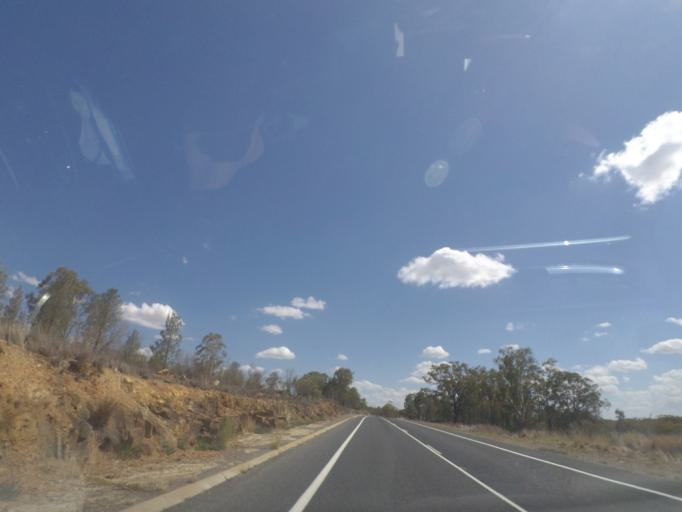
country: AU
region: Queensland
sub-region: Southern Downs
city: Warwick
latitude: -28.2250
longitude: 151.5525
